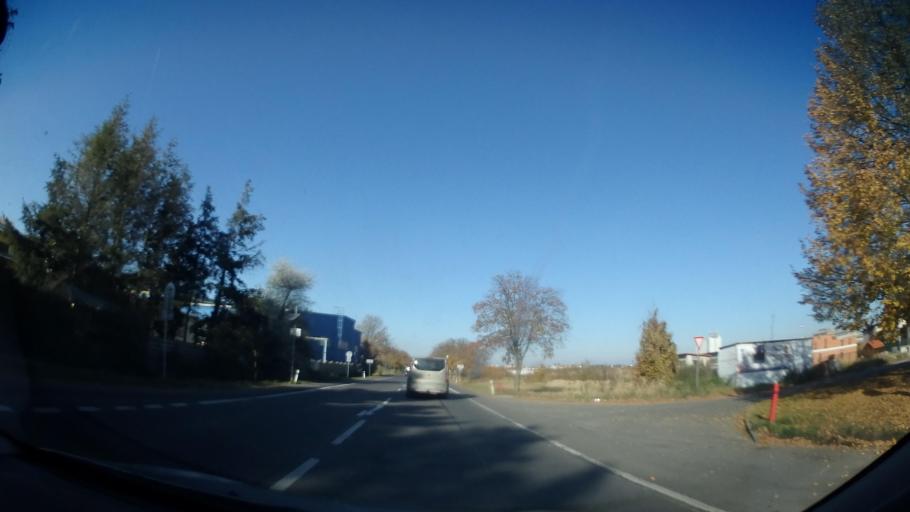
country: CZ
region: Pardubicky
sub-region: Okres Chrudim
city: Slatinany
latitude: 49.9218
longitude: 15.8072
